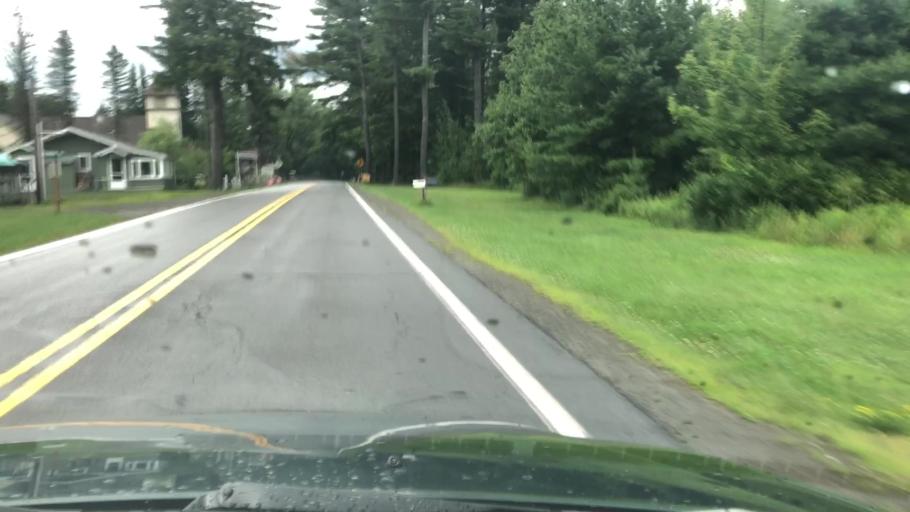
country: US
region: Pennsylvania
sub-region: Monroe County
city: Mountainhome
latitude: 41.3129
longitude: -75.2104
